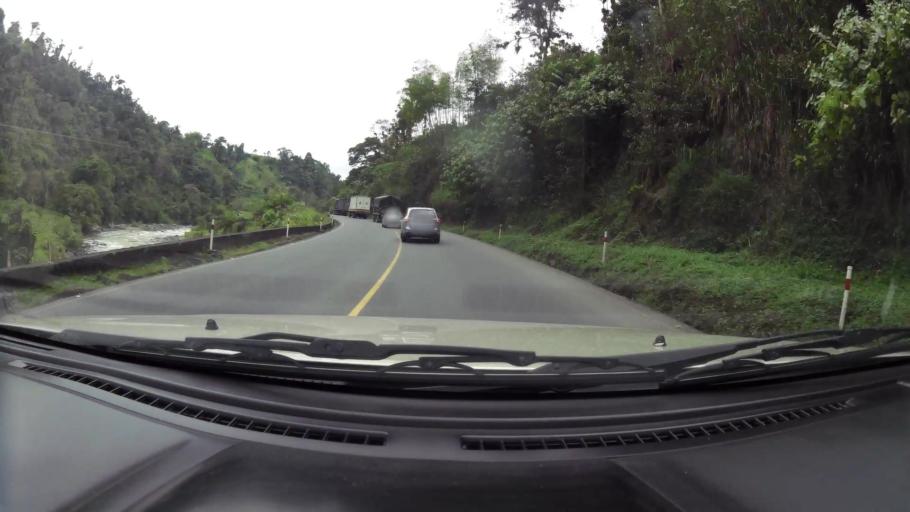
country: EC
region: Santo Domingo de los Tsachilas
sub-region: Canton Santo Domingo de los Colorados
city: Santo Domingo de los Colorados
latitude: -0.3190
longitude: -79.0084
